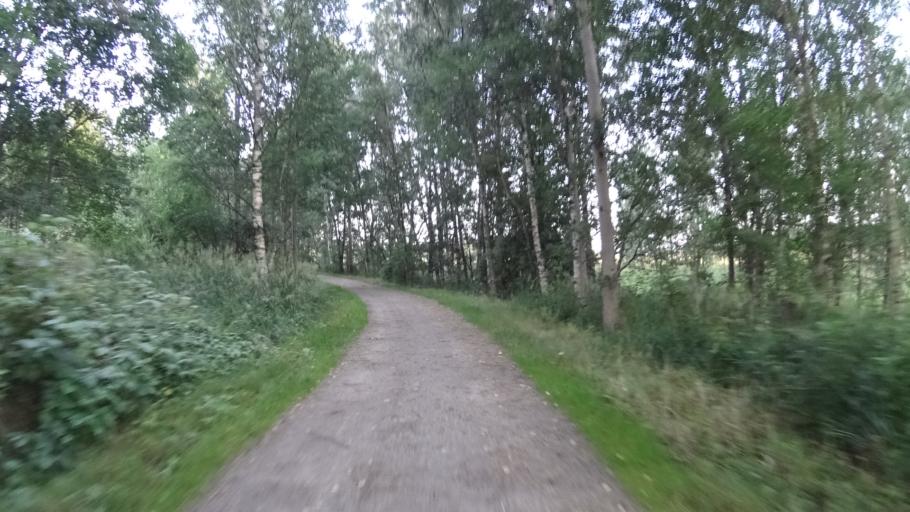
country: FI
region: Uusimaa
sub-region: Helsinki
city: Teekkarikylae
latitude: 60.2105
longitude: 24.8434
